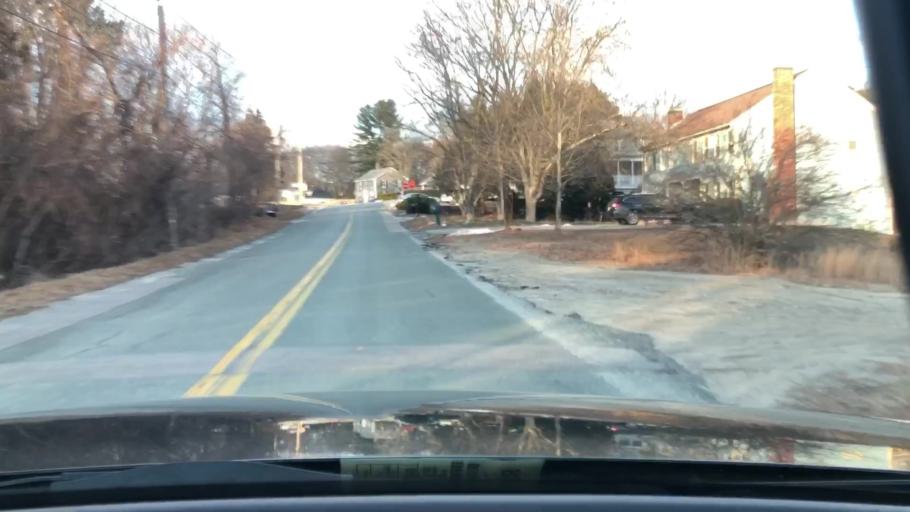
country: US
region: Massachusetts
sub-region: Worcester County
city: Millville
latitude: 42.0156
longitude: -71.5820
